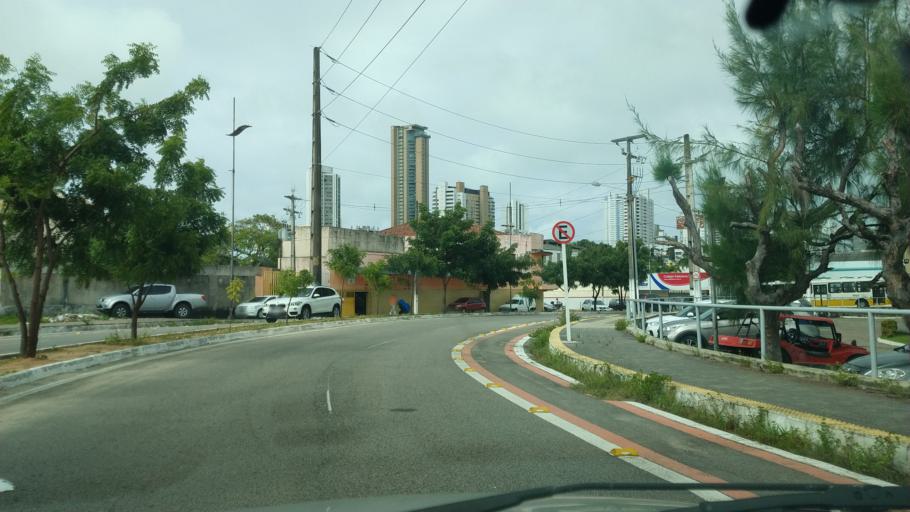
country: BR
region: Rio Grande do Norte
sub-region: Natal
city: Natal
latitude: -5.7808
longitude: -35.2068
